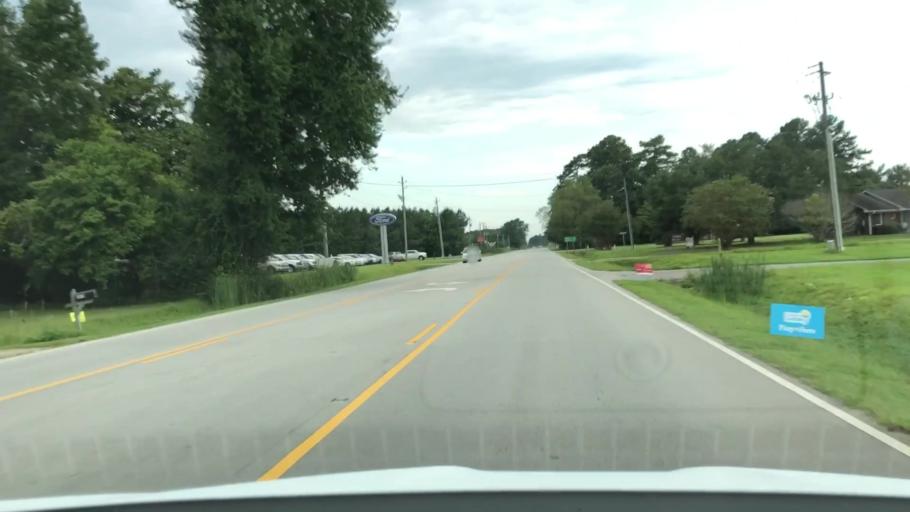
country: US
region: North Carolina
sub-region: Jones County
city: Trenton
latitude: 35.0664
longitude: -77.3620
